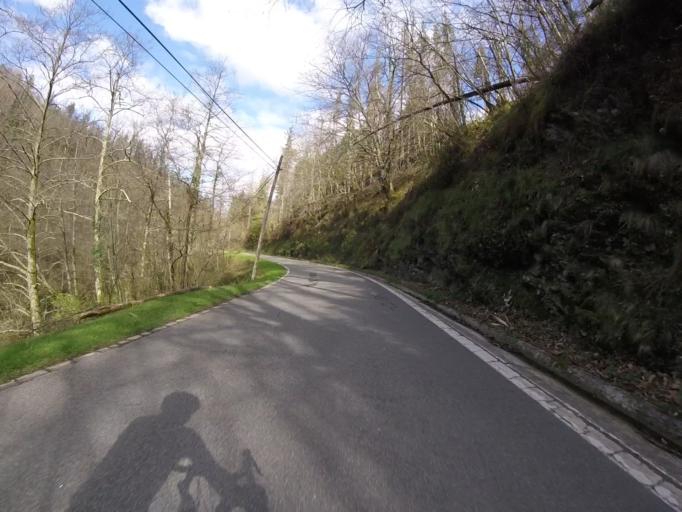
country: ES
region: Navarre
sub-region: Provincia de Navarra
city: Goizueta
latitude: 43.1586
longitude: -1.8494
